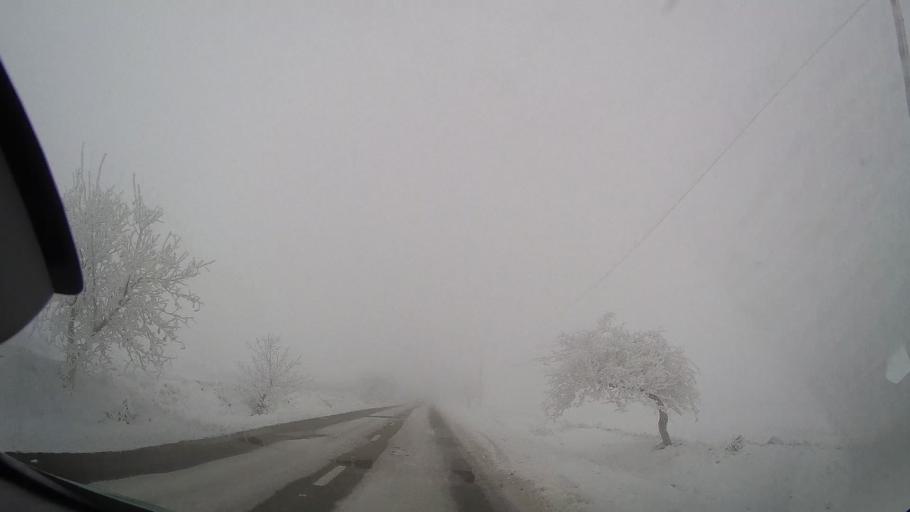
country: RO
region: Neamt
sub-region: Comuna Valea Ursului
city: Valea Ursului
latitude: 46.8030
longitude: 27.0732
